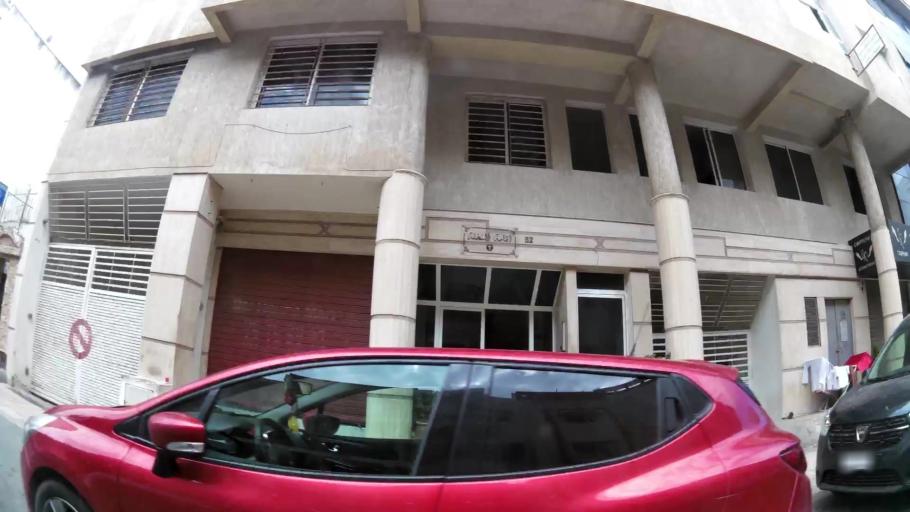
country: MA
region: Gharb-Chrarda-Beni Hssen
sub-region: Kenitra Province
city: Kenitra
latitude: 34.2581
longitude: -6.5871
